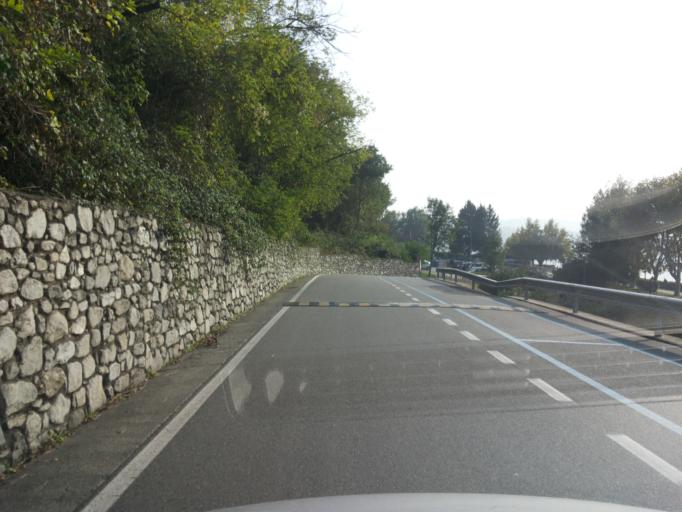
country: IT
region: Piedmont
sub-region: Provincia di Biella
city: Viverone
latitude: 45.4139
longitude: 8.0489
